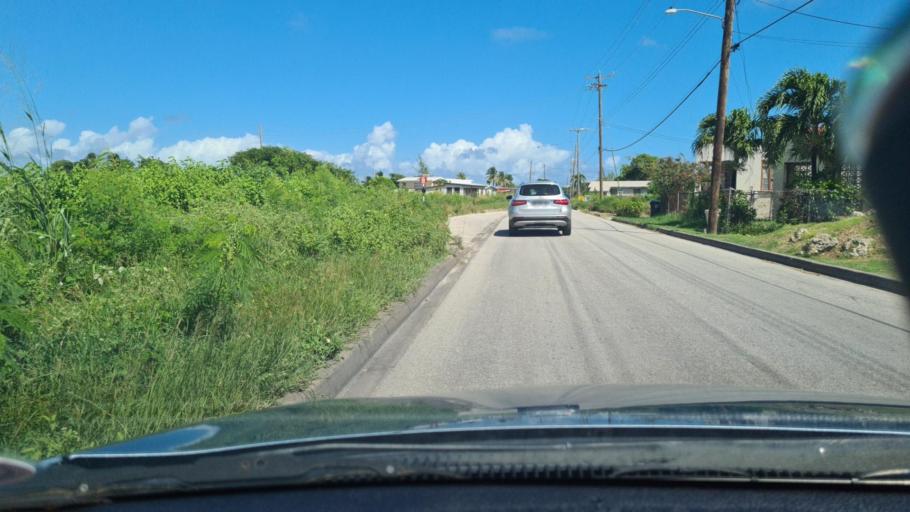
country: BB
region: Saint Philip
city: Crane
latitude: 13.1321
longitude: -59.4393
